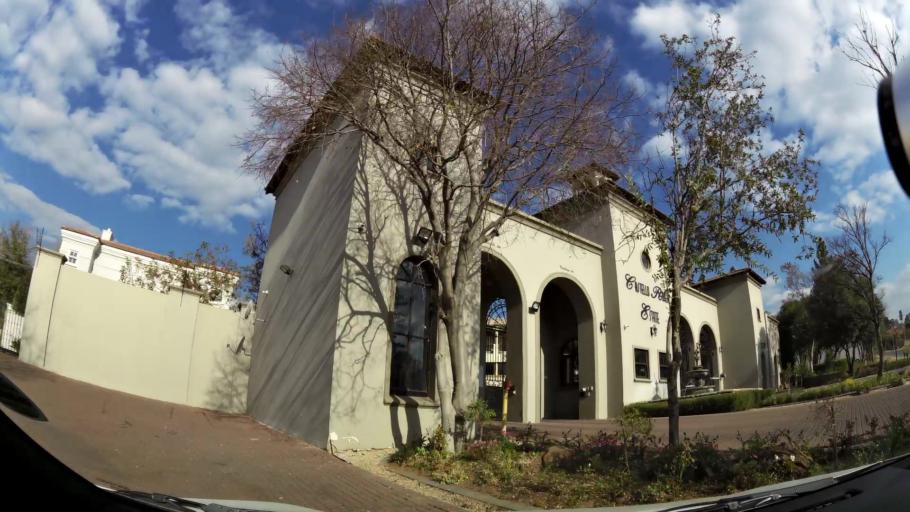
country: ZA
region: Gauteng
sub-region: City of Johannesburg Metropolitan Municipality
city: Diepsloot
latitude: -25.9991
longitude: 28.0263
